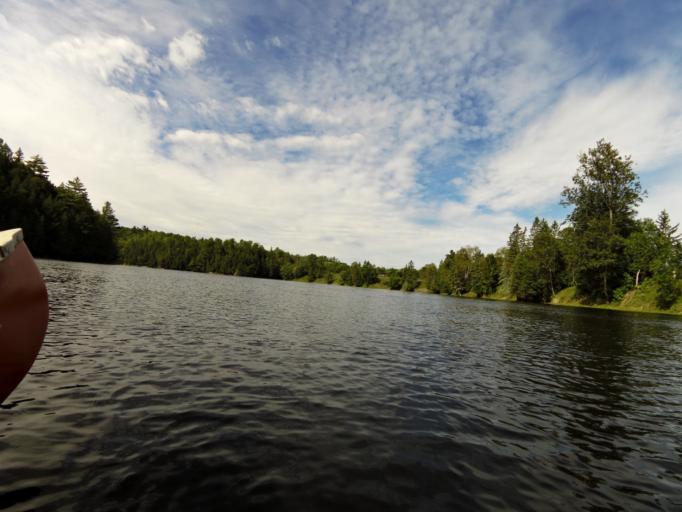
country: CA
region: Quebec
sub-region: Outaouais
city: Wakefield
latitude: 45.7907
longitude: -75.9446
